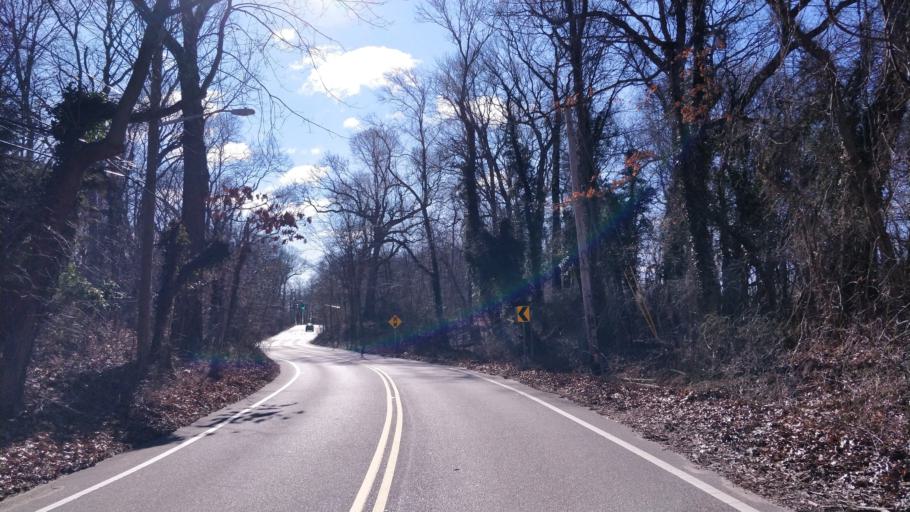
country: US
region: New York
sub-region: Suffolk County
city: Stony Brook
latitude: 40.9036
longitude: -73.1322
